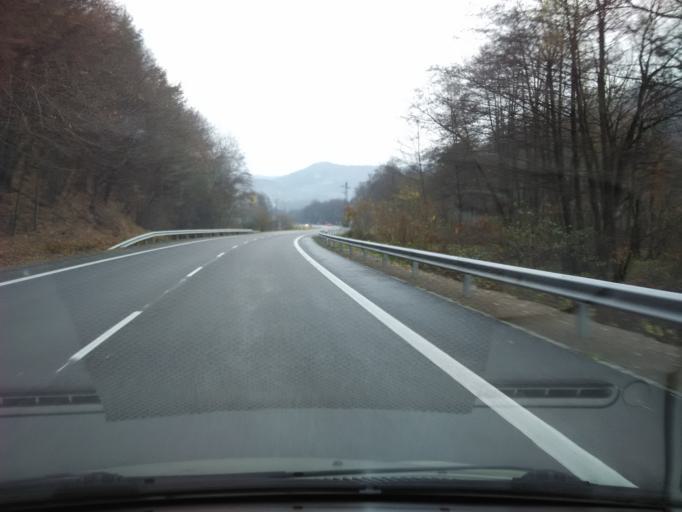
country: SK
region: Banskobystricky
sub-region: Okres Ziar nad Hronom
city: Kremnica
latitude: 48.6431
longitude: 18.9041
